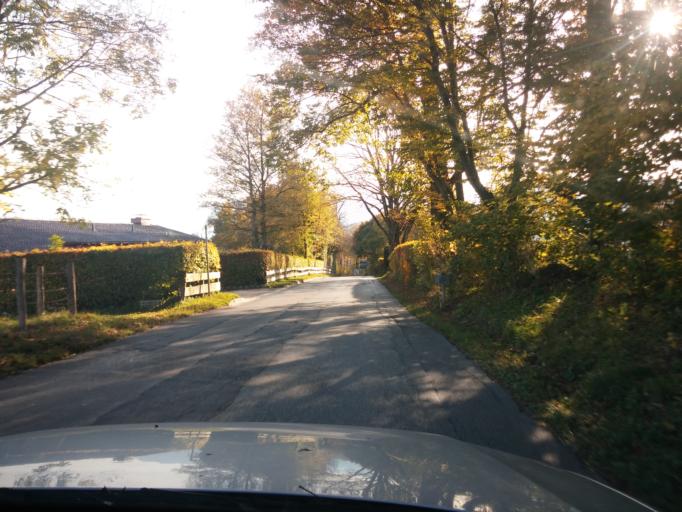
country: DE
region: Bavaria
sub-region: Upper Bavaria
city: Bad Toelz
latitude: 47.7659
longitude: 11.5695
